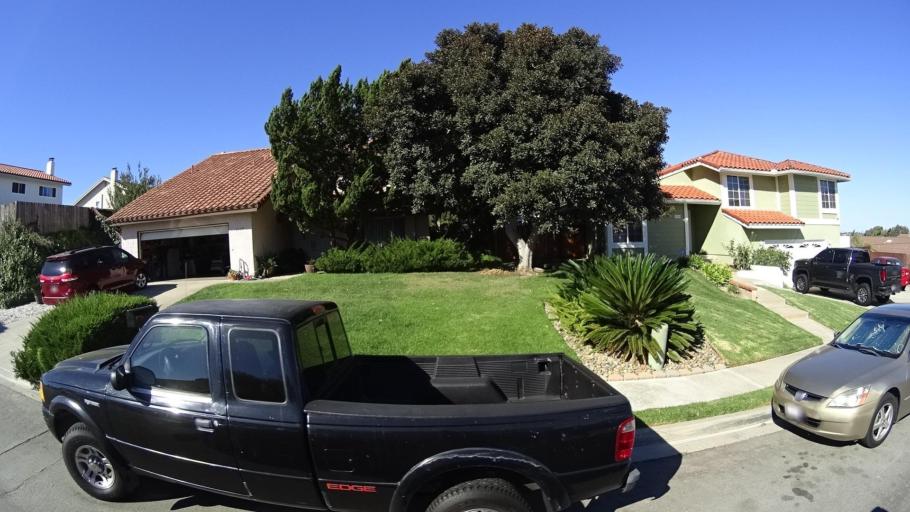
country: US
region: California
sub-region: San Diego County
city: Bonita
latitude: 32.6620
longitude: -116.9971
